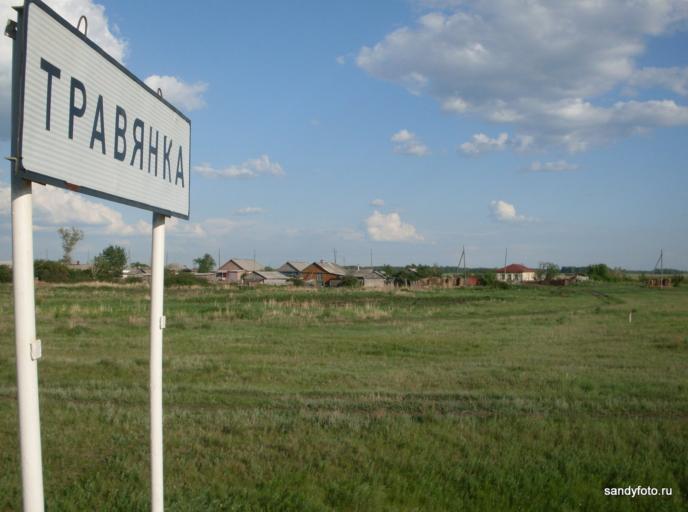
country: RU
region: Chelyabinsk
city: Bobrovka
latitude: 54.1617
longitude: 61.8142
